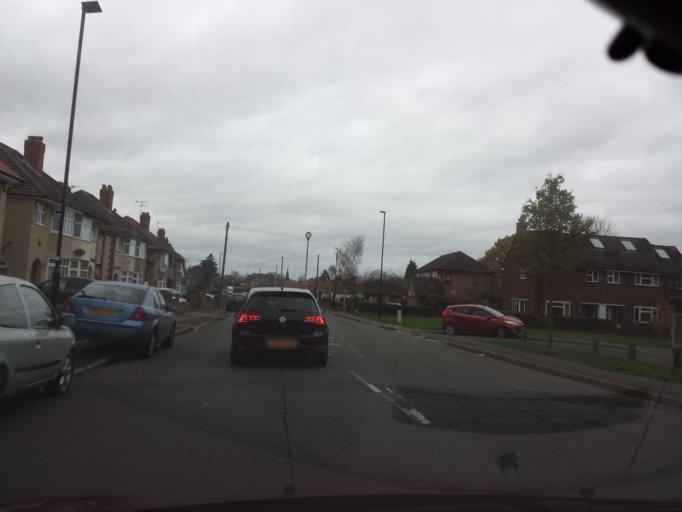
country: GB
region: England
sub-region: Greater London
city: Feltham
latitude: 51.4338
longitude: -0.4185
